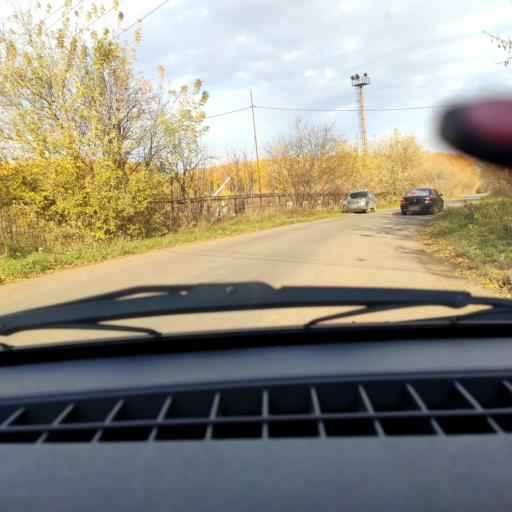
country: RU
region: Bashkortostan
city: Ufa
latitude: 54.7857
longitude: 56.1610
